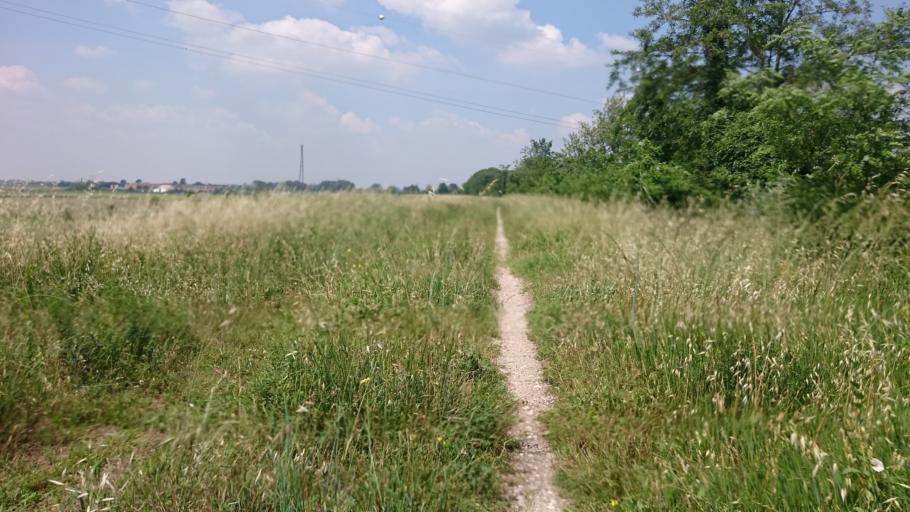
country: IT
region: Lombardy
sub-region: Provincia di Mantova
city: San Biagio
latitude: 45.1229
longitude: 10.8505
